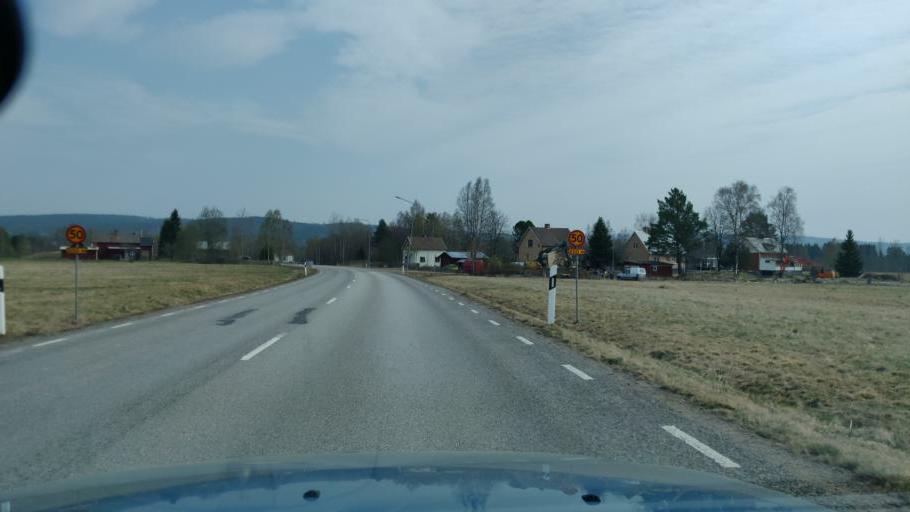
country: SE
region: Vaermland
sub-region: Munkfors Kommun
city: Munkfors
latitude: 59.8330
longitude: 13.5100
